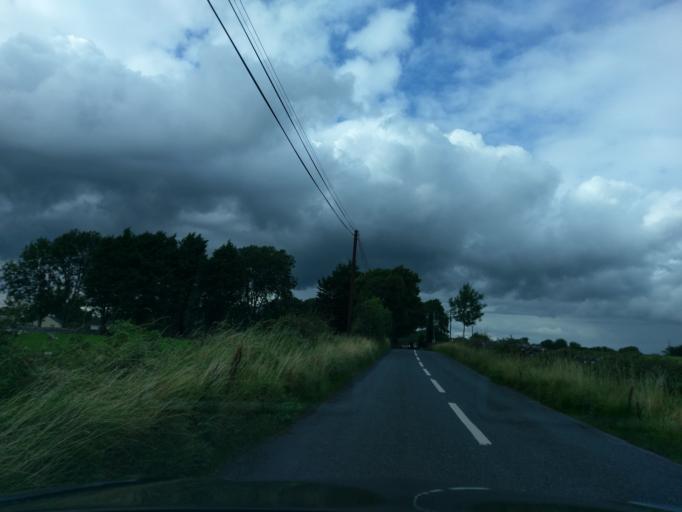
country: IE
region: Connaught
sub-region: County Galway
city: Athenry
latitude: 53.2735
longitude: -8.7431
